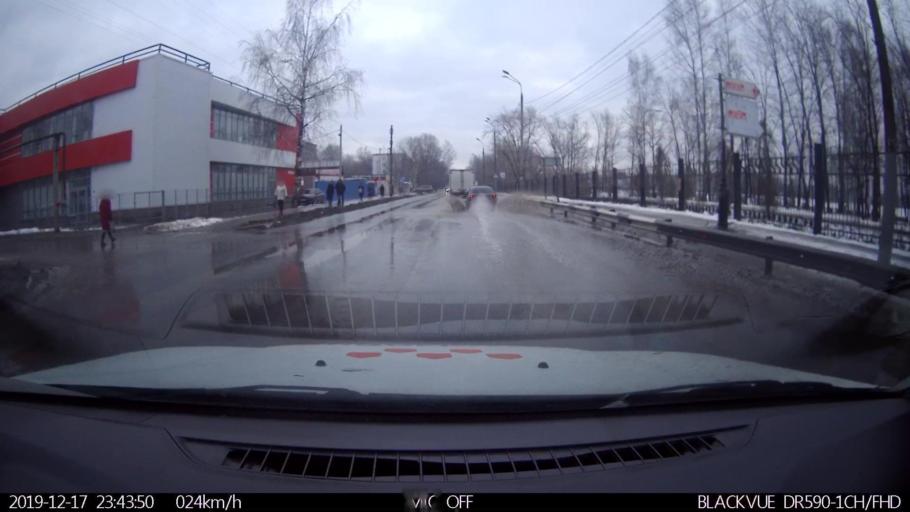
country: RU
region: Nizjnij Novgorod
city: Gorbatovka
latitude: 56.3589
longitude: 43.8268
